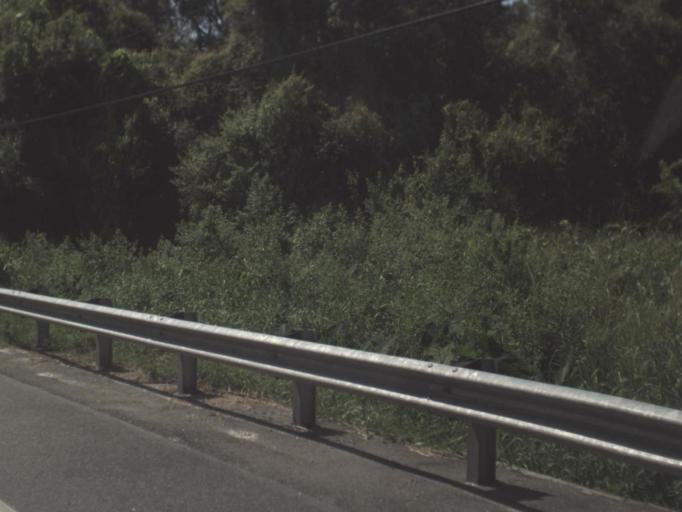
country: US
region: Florida
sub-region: Hillsborough County
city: Dover
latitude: 28.0152
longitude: -82.2482
